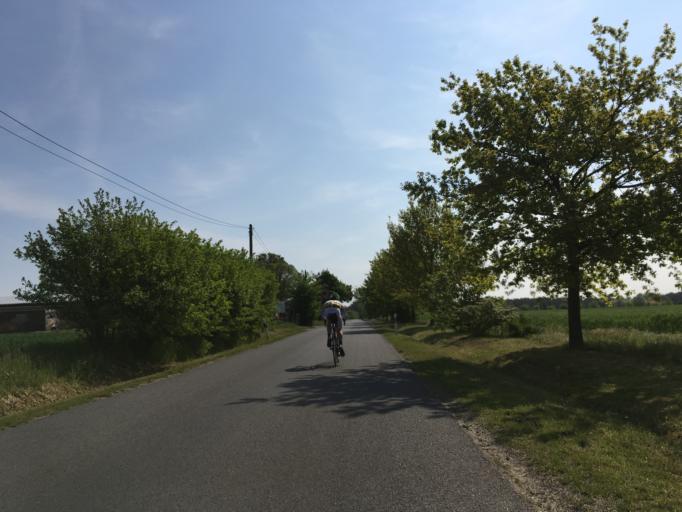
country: DE
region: Berlin
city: Hellersdorf
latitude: 52.5694
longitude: 13.6358
